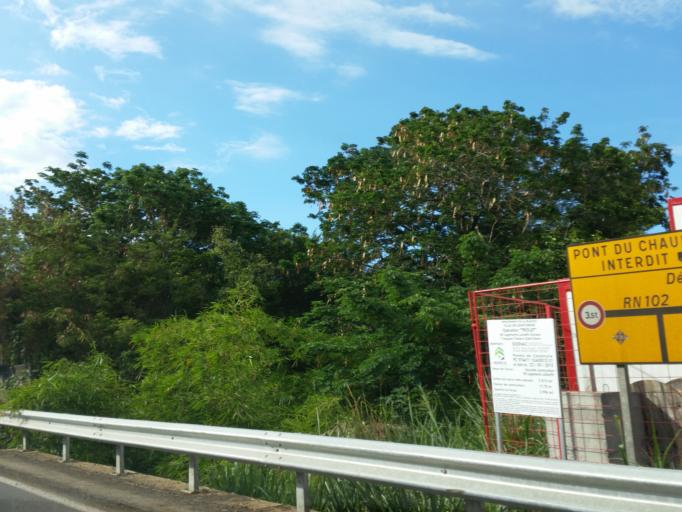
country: RE
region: Reunion
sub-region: Reunion
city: Sainte-Marie
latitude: -20.9004
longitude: 55.4995
